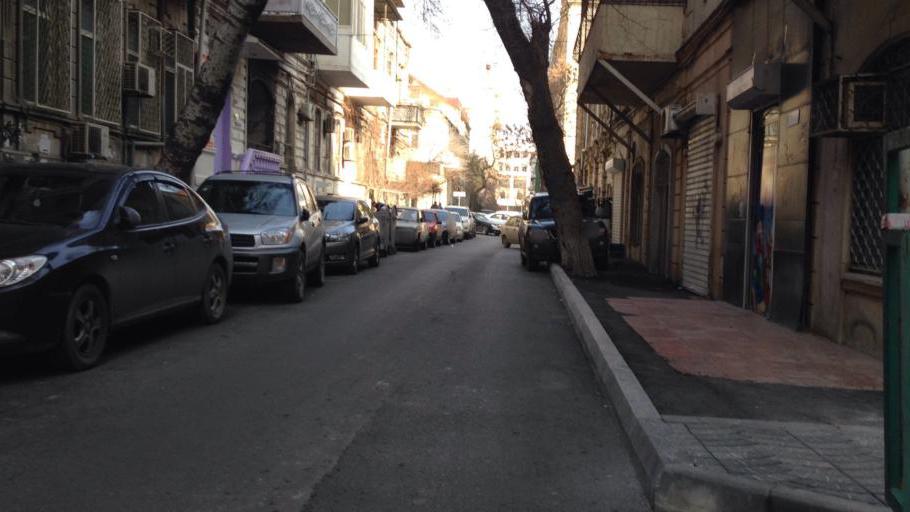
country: AZ
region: Baki
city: Badamdar
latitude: 40.3746
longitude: 49.8404
